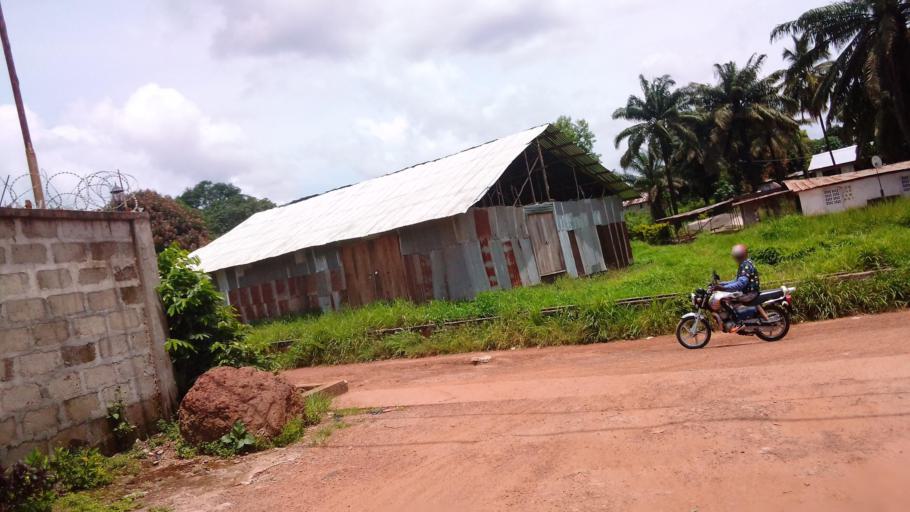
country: SL
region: Northern Province
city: Makeni
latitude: 8.8722
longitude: -12.0369
